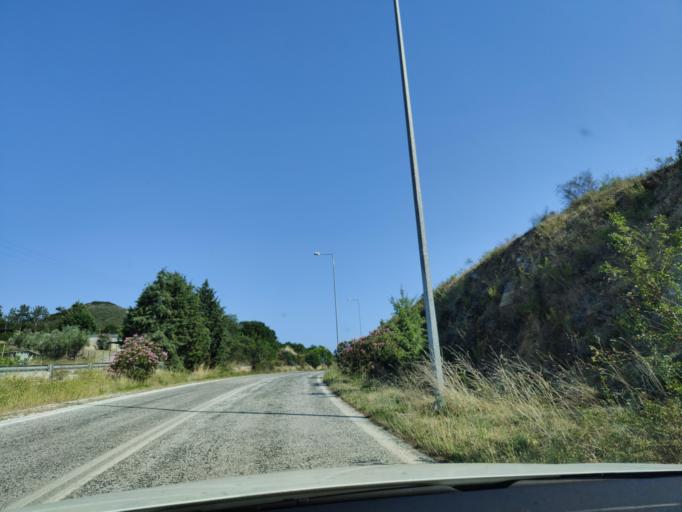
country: GR
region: East Macedonia and Thrace
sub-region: Nomos Kavalas
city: Nea Iraklitsa
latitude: 40.8647
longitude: 24.3000
